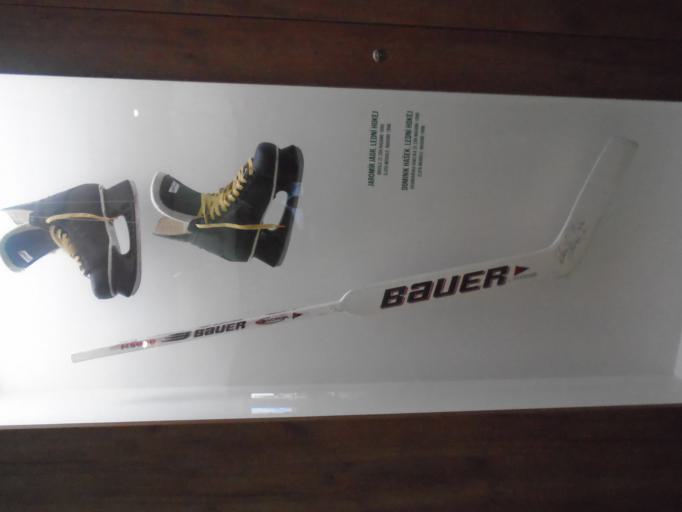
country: CZ
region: Moravskoslezsky
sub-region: Okres Ostrava-Mesto
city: Ostrava
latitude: 49.8052
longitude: 18.2485
